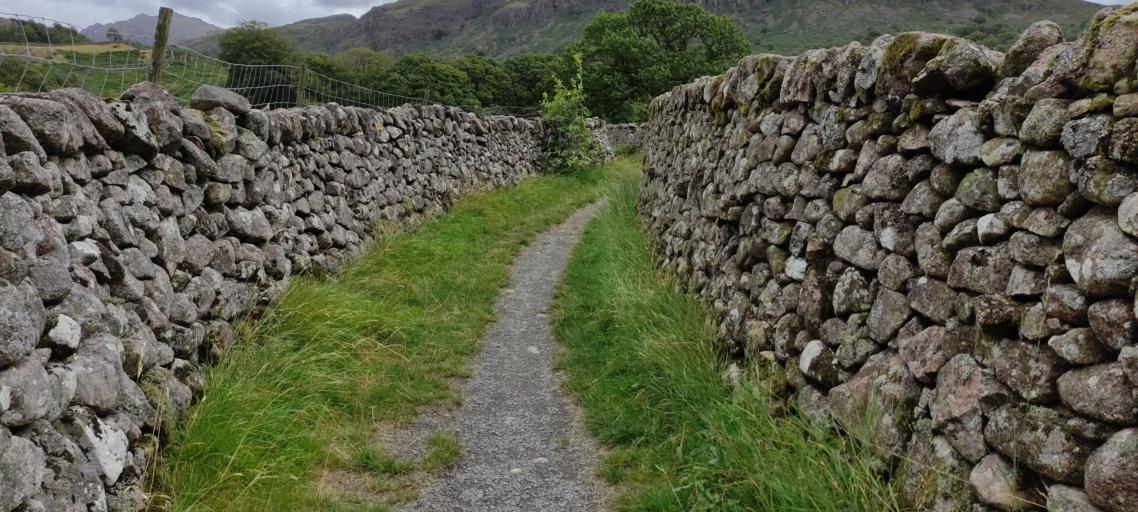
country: GB
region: England
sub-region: Cumbria
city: Millom
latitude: 54.3922
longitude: -3.2715
